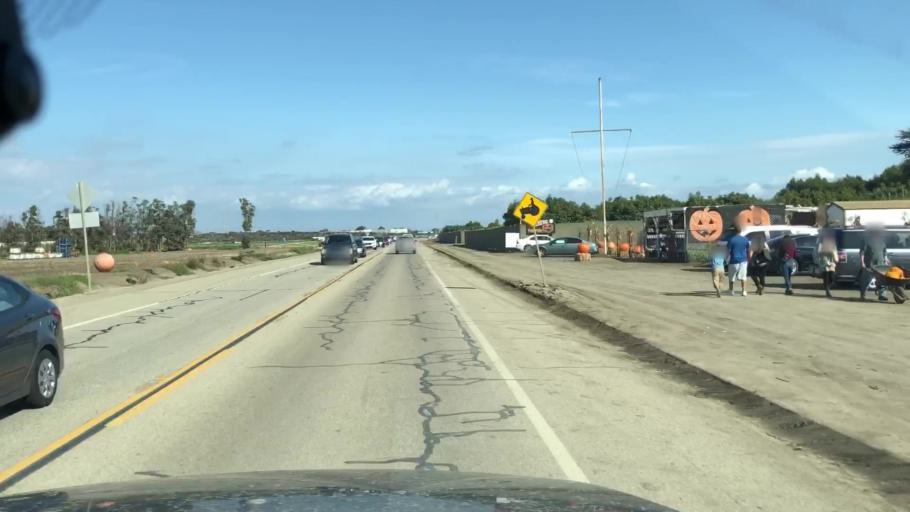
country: US
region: California
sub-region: Ventura County
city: Oxnard Shores
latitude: 34.2451
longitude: -119.2254
